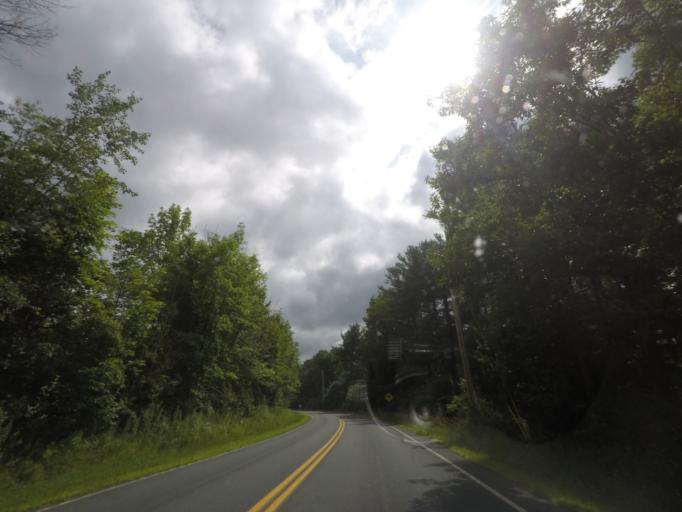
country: US
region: New York
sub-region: Saratoga County
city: Stillwater
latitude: 42.8859
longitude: -73.5617
